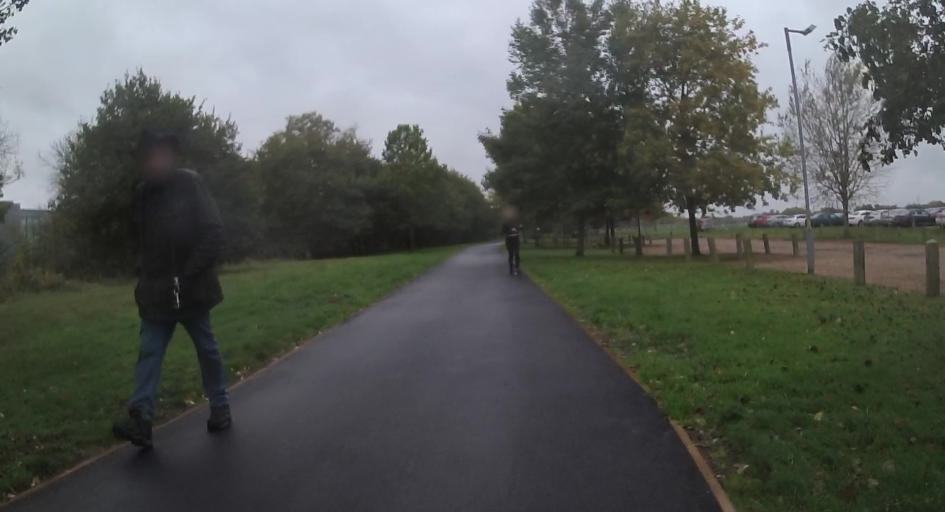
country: GB
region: England
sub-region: Surrey
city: Byfleet
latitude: 51.3523
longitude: -0.4663
